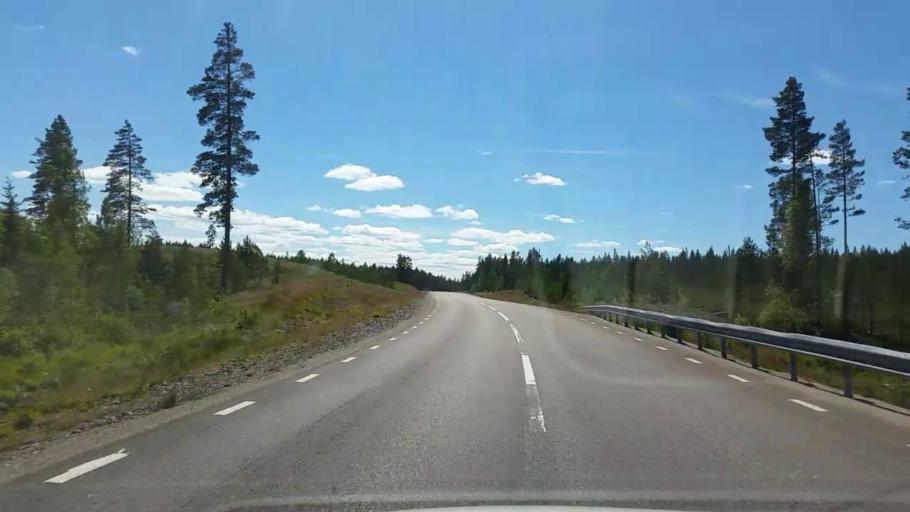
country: SE
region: Gaevleborg
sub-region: Bollnas Kommun
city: Vittsjo
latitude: 61.0951
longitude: 15.8272
